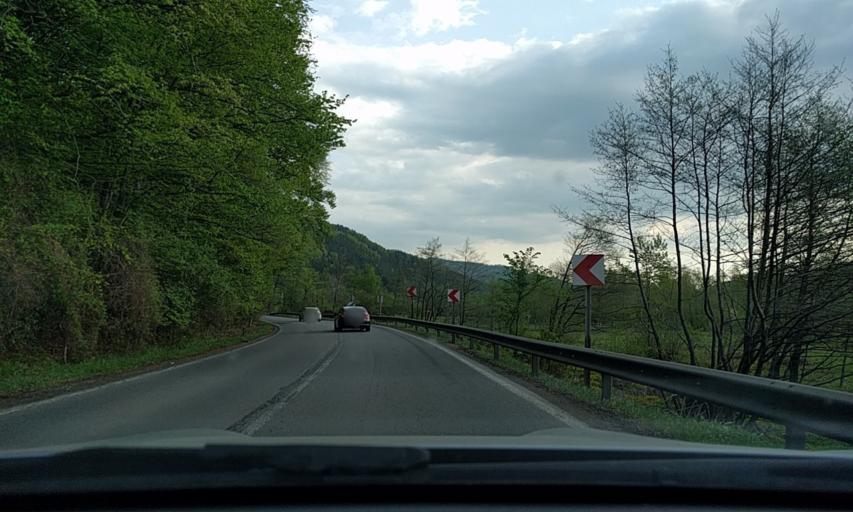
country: RO
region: Bacau
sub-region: Oras Slanic-Moldova
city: Slanic-Moldova
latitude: 46.1559
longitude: 26.4605
